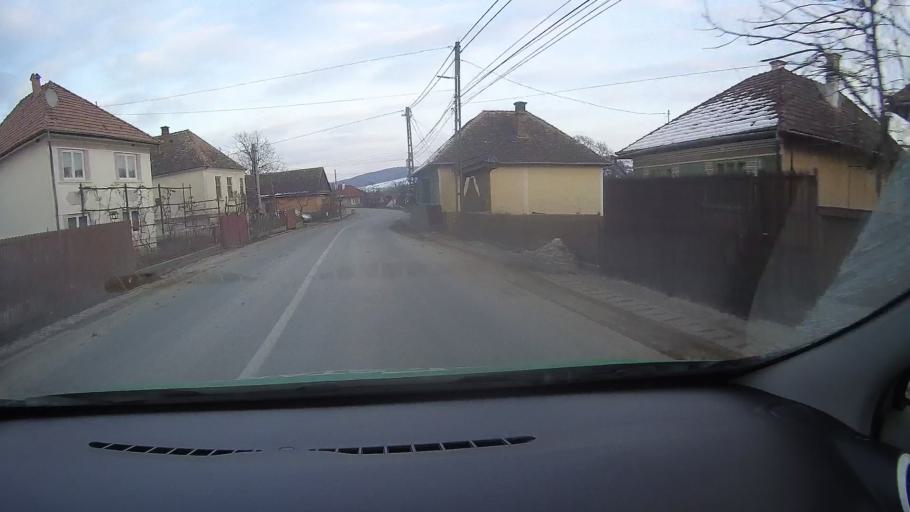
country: RO
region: Harghita
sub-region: Comuna Simonesti
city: Simonesti
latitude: 46.3570
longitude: 25.1516
